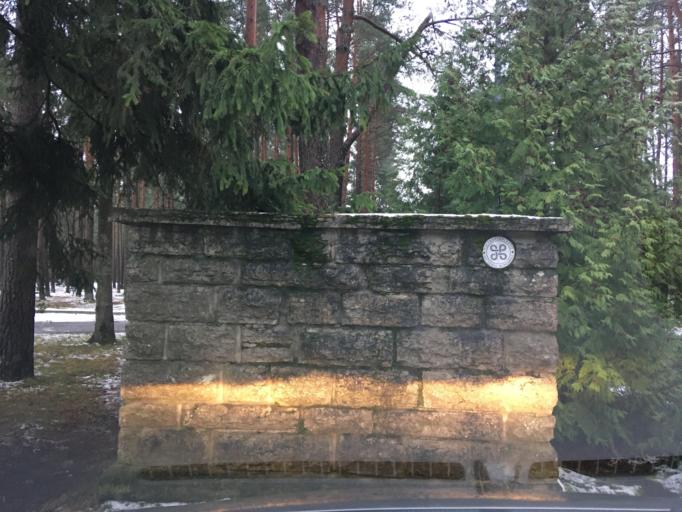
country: EE
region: Harju
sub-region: Tallinna linn
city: Tallinn
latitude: 59.3806
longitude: 24.7288
